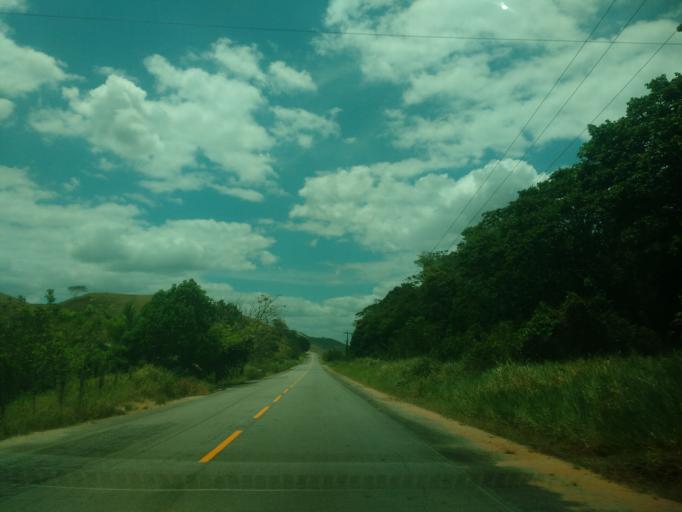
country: BR
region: Alagoas
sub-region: Uniao Dos Palmares
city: Uniao dos Palmares
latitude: -9.1425
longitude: -36.0526
